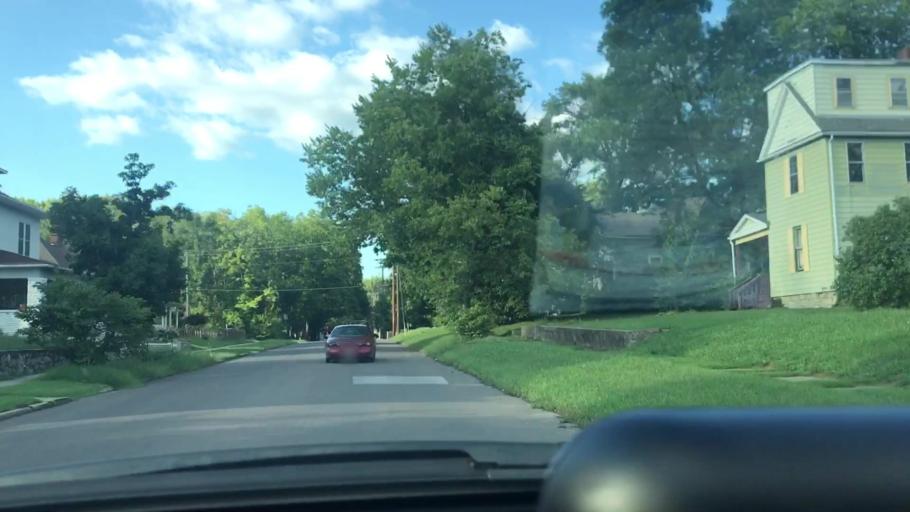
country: US
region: Missouri
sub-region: Pettis County
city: Sedalia
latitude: 38.7028
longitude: -93.2365
